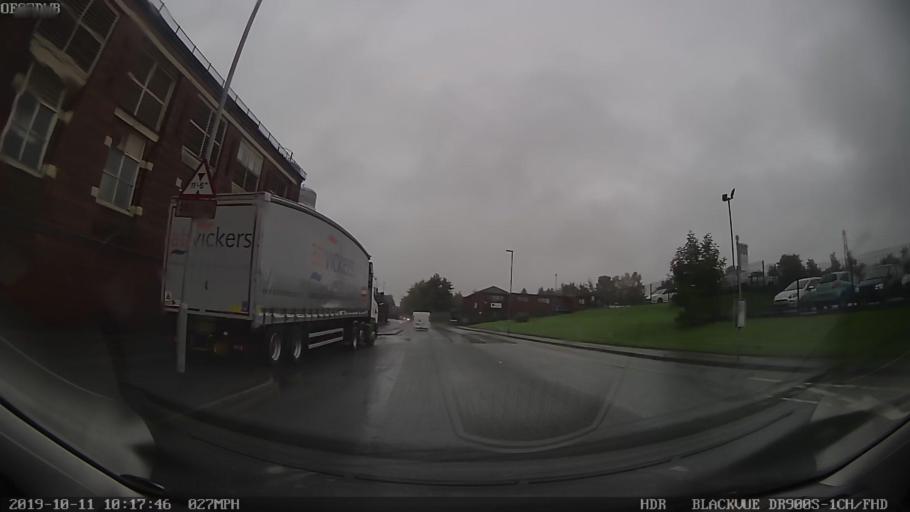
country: GB
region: England
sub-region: Borough of Rochdale
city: Middleton
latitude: 53.5420
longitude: -2.1726
